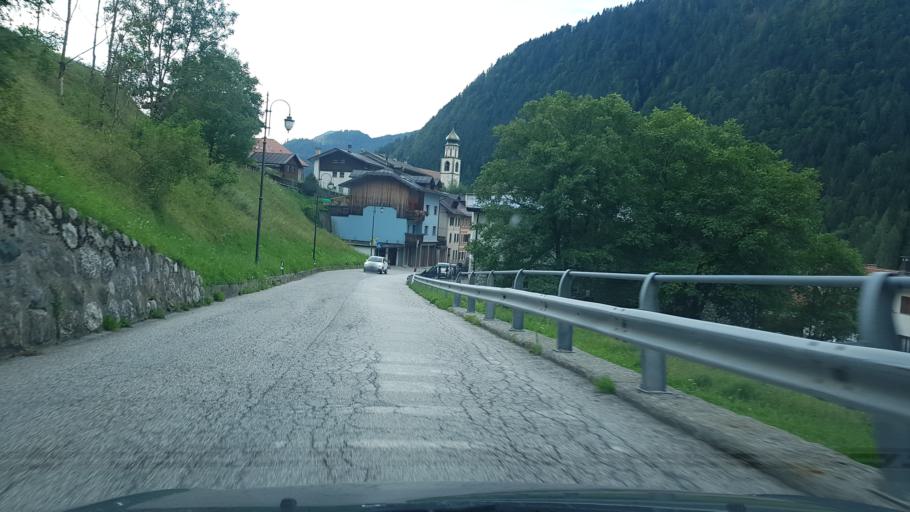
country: IT
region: Friuli Venezia Giulia
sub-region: Provincia di Udine
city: Forni Avoltri
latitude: 46.5874
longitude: 12.7756
